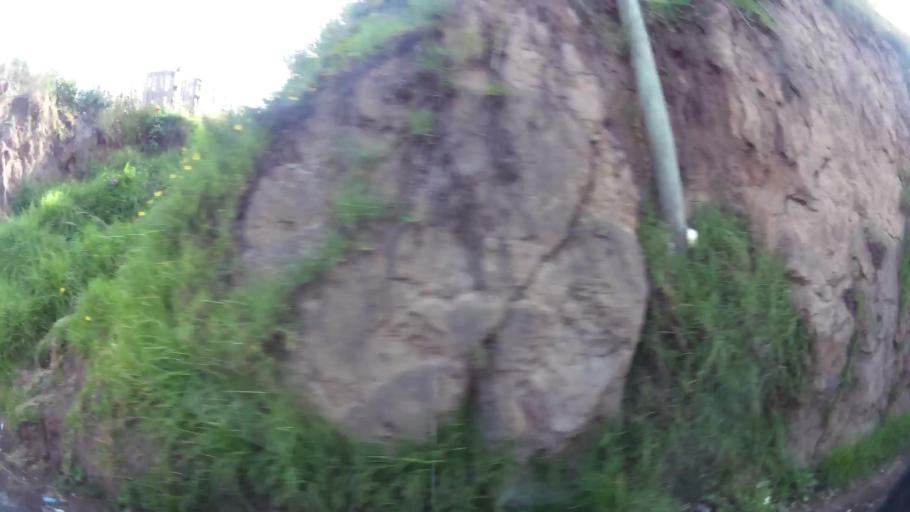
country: EC
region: Pichincha
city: Quito
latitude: -0.1395
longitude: -78.4594
